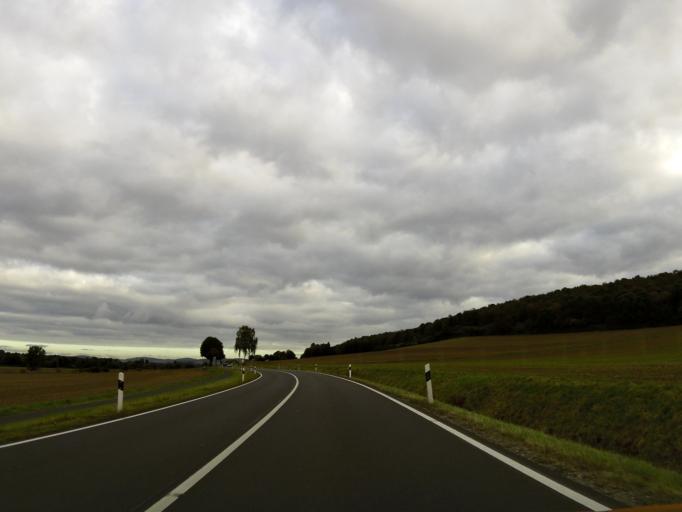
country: DE
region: Lower Saxony
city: Norten-Hardenberg
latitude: 51.6511
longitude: 9.9529
